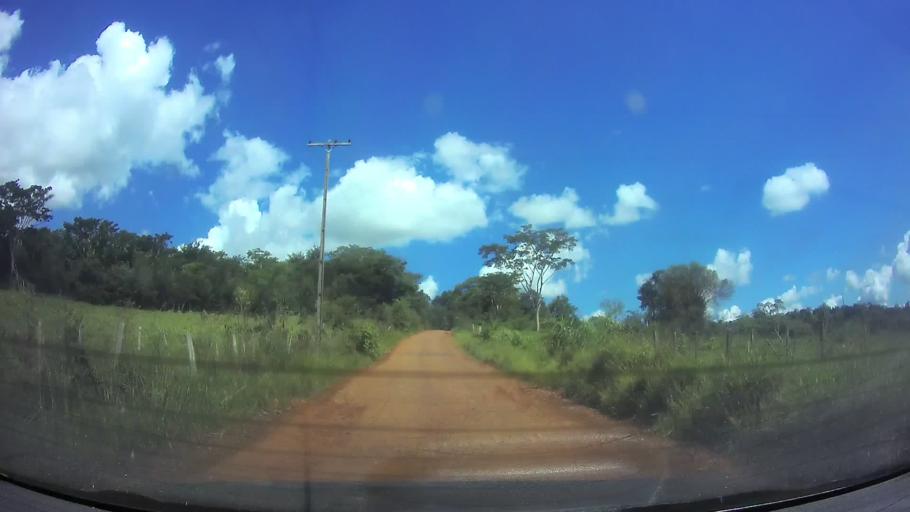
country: PY
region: Paraguari
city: La Colmena
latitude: -25.9392
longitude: -56.7804
